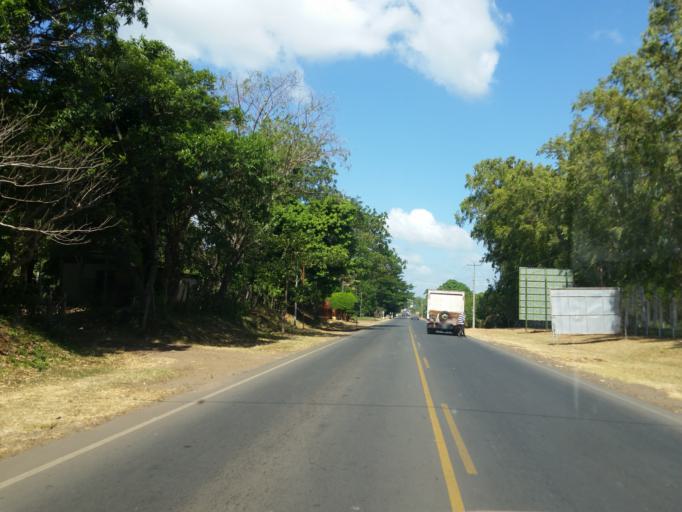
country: NI
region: Granada
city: Nandaime
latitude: 11.7678
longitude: -86.0499
